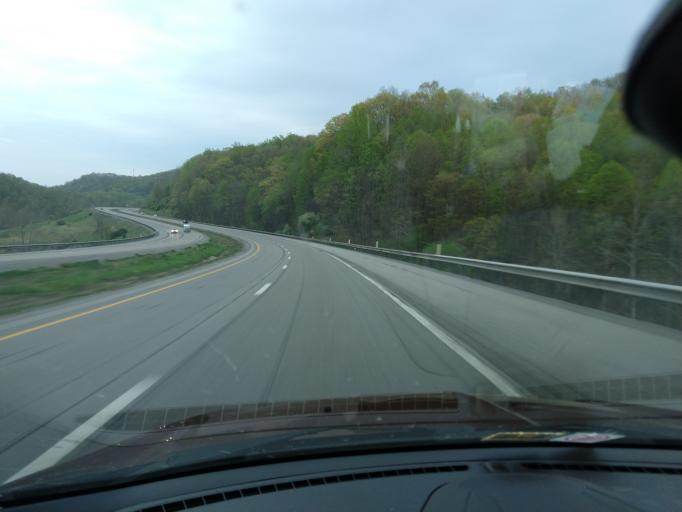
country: US
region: West Virginia
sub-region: Lewis County
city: Weston
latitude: 38.9171
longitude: -80.5615
